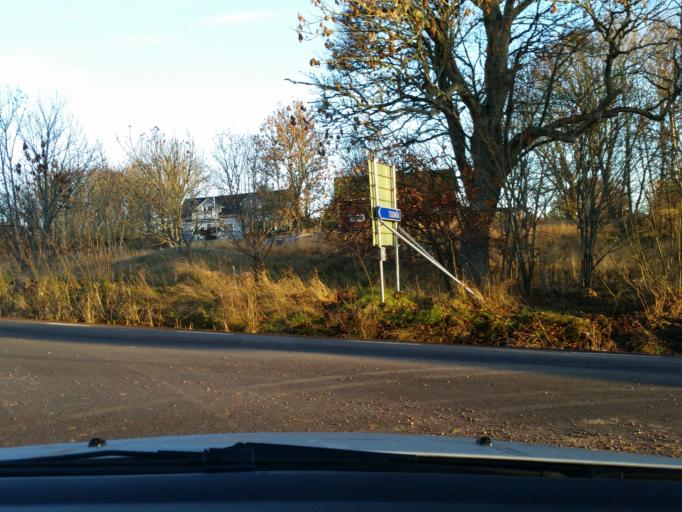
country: AX
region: Alands landsbygd
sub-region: Sund
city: Sund
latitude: 60.2352
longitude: 20.0760
